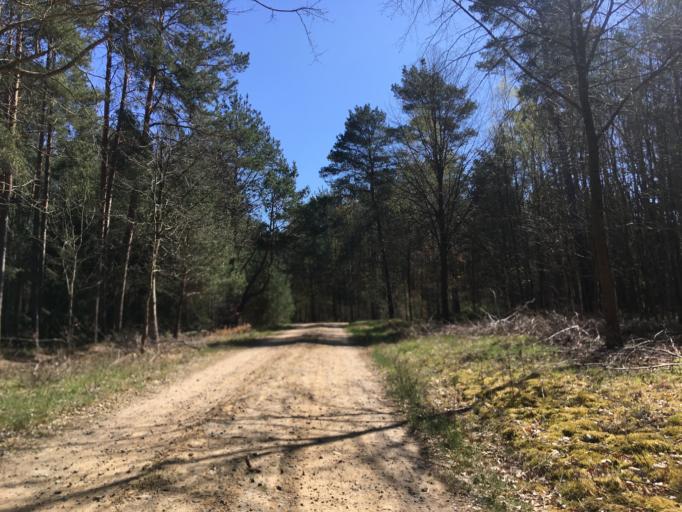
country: DE
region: Brandenburg
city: Wandlitz
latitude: 52.7045
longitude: 13.5171
